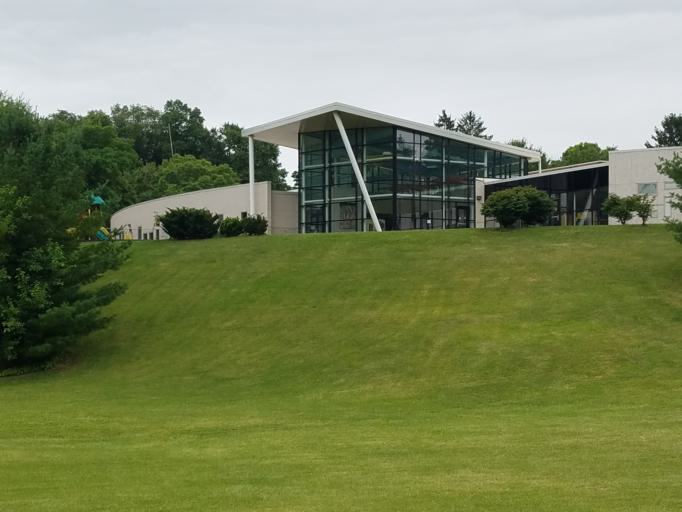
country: US
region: Ohio
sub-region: Morrow County
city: Mount Gilead
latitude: 40.5530
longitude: -82.8227
